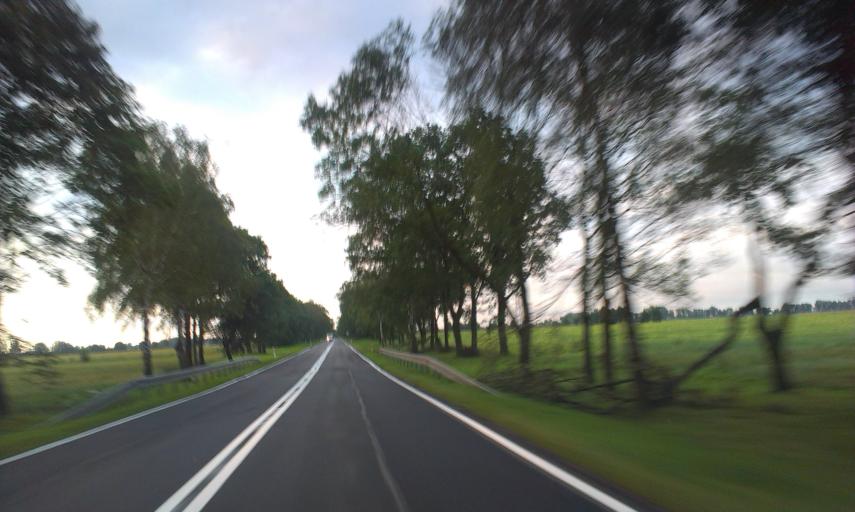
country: PL
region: Greater Poland Voivodeship
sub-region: Powiat zlotowski
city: Okonek
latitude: 53.6161
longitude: 16.7878
